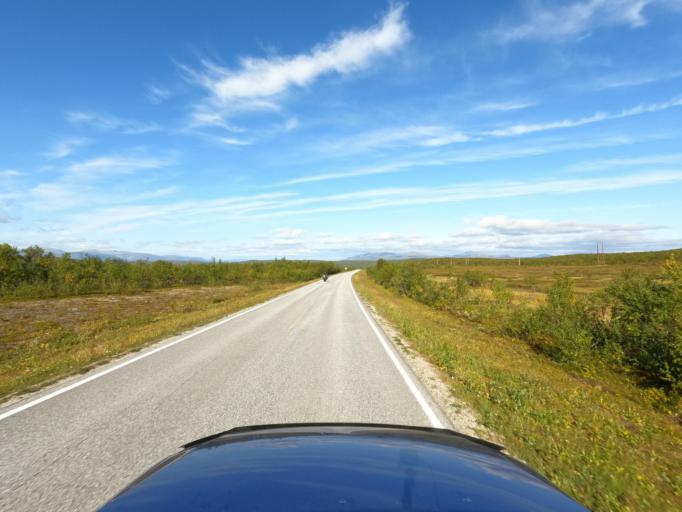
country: NO
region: Finnmark Fylke
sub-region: Karasjok
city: Karasjohka
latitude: 69.7266
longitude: 25.2347
